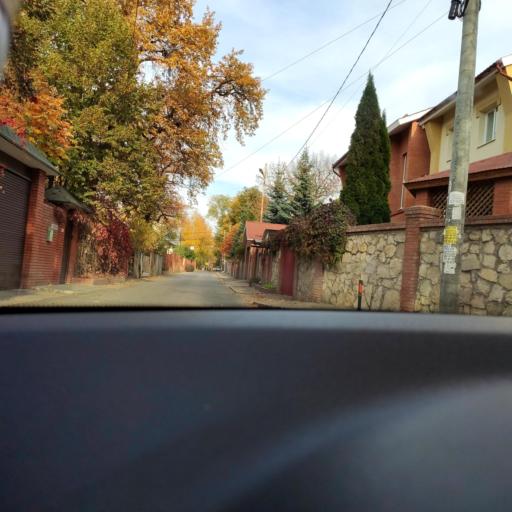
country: RU
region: Samara
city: Samara
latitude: 53.2729
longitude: 50.1933
